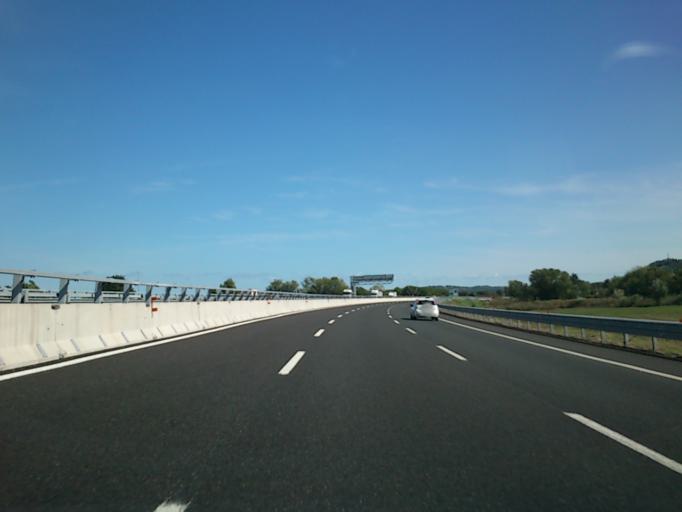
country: IT
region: The Marches
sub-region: Provincia di Pesaro e Urbino
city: Pesaro
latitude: 43.8994
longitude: 12.8638
